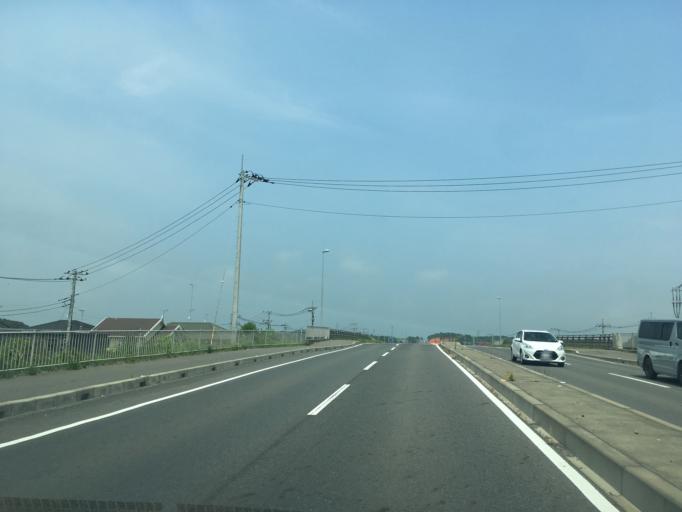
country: JP
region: Ibaraki
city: Oarai
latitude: 36.3517
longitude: 140.5802
